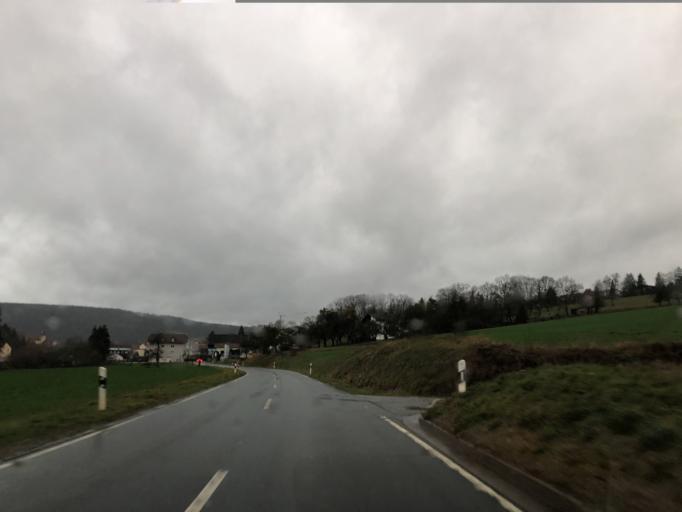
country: DE
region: Hesse
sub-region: Regierungsbezirk Darmstadt
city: Bad Konig
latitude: 49.7423
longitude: 9.0214
